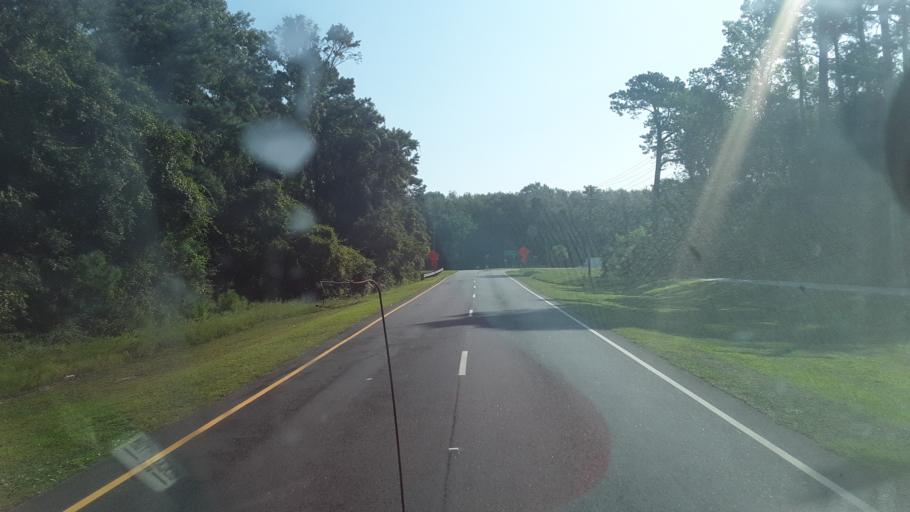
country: US
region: South Carolina
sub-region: Horry County
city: North Myrtle Beach
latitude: 33.8454
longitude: -78.6534
